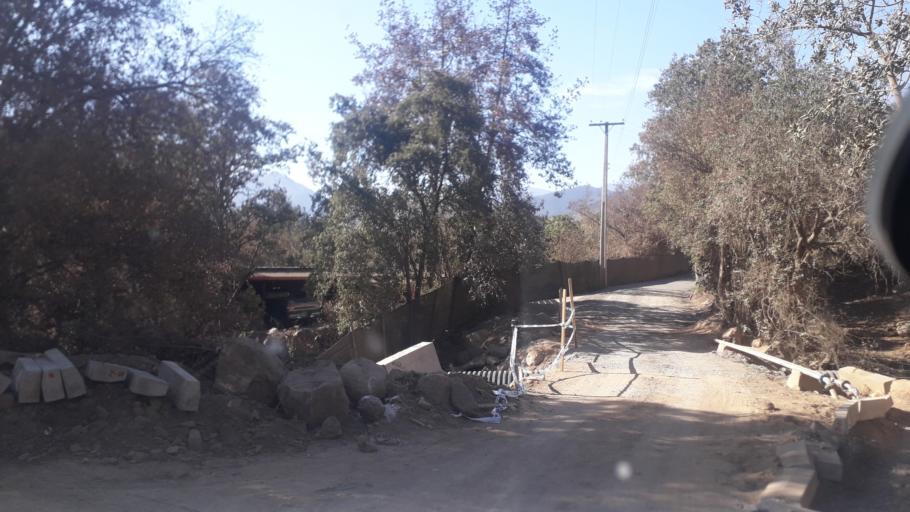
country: CL
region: Valparaiso
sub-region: Provincia de Marga Marga
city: Limache
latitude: -33.0780
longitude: -71.1003
